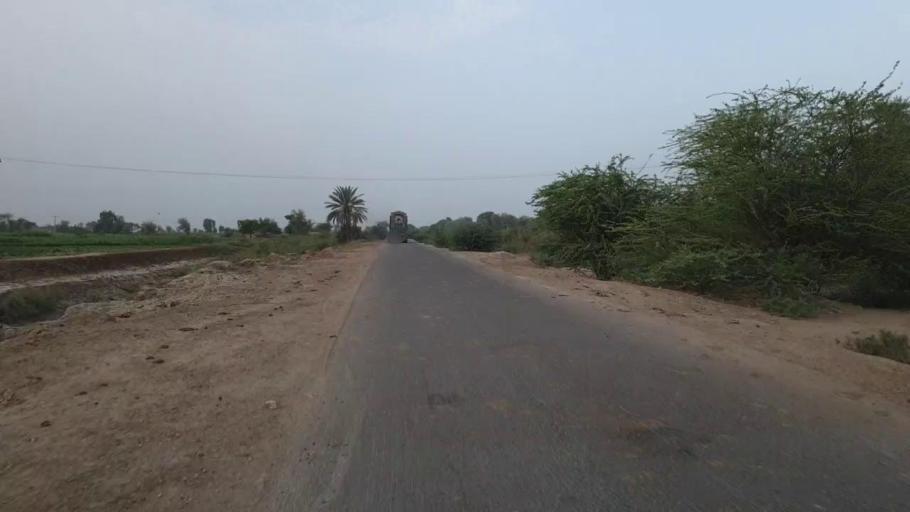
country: PK
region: Sindh
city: Daur
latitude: 26.4342
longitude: 68.2695
